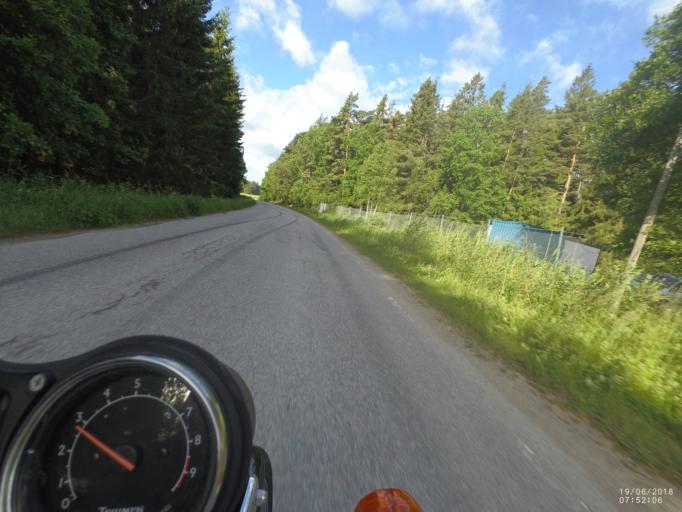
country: SE
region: Soedermanland
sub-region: Nykopings Kommun
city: Nykoping
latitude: 58.7795
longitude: 17.0221
